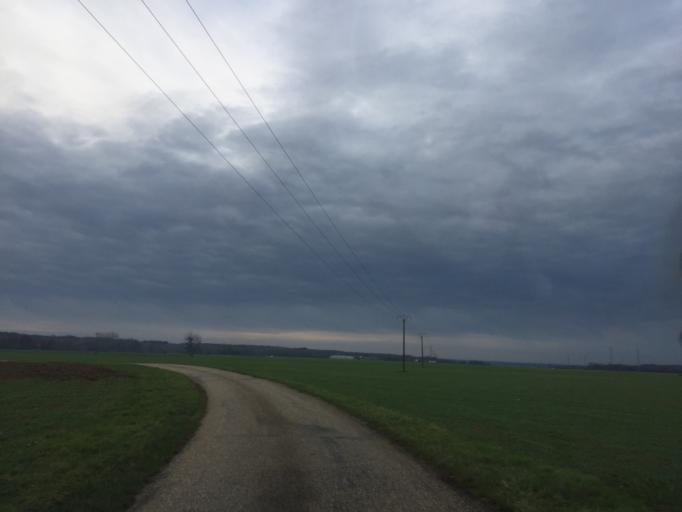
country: FR
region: Franche-Comte
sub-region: Departement du Jura
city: Mont-sous-Vaudrey
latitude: 46.9423
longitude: 5.6717
